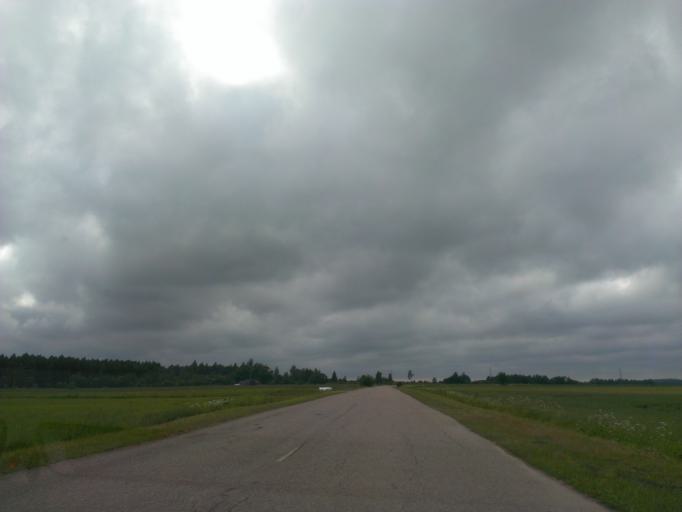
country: LV
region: Aizpute
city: Aizpute
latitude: 56.7169
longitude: 21.4557
